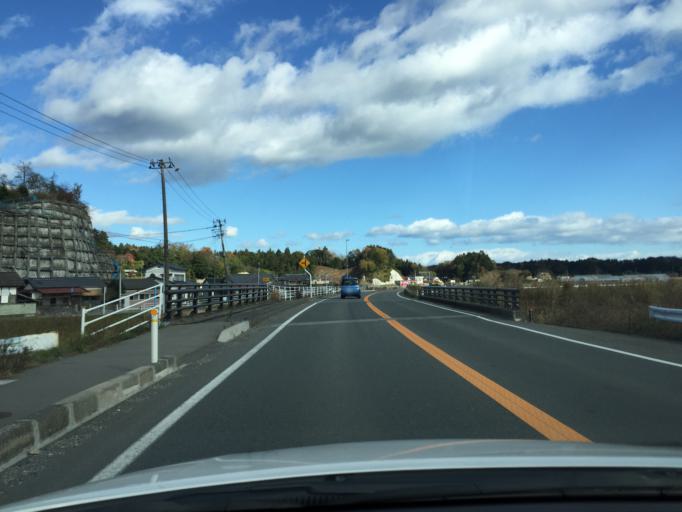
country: JP
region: Fukushima
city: Namie
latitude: 37.5233
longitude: 140.9983
